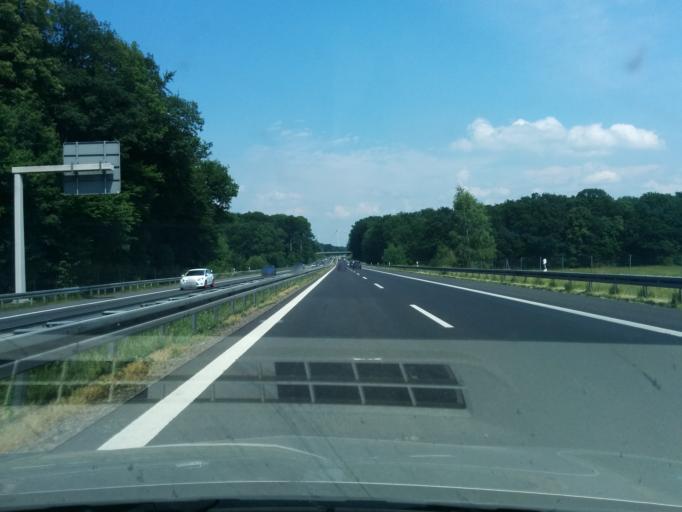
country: DE
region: Brandenburg
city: Gramzow
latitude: 53.1928
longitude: 13.9377
